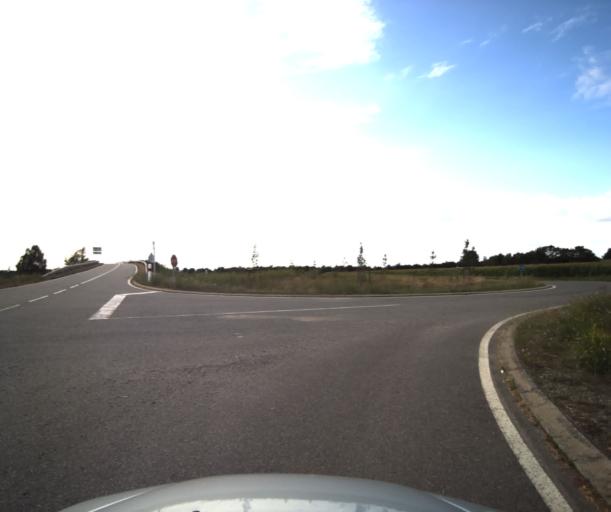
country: FR
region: Midi-Pyrenees
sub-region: Departement de la Haute-Garonne
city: Le Fauga
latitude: 43.4162
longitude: 1.3010
